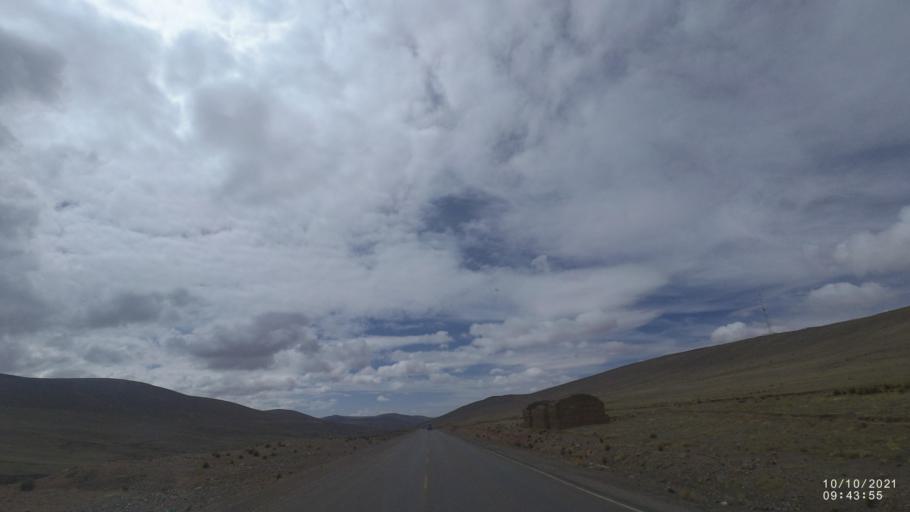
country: BO
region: La Paz
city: Quime
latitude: -17.1551
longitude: -67.3428
